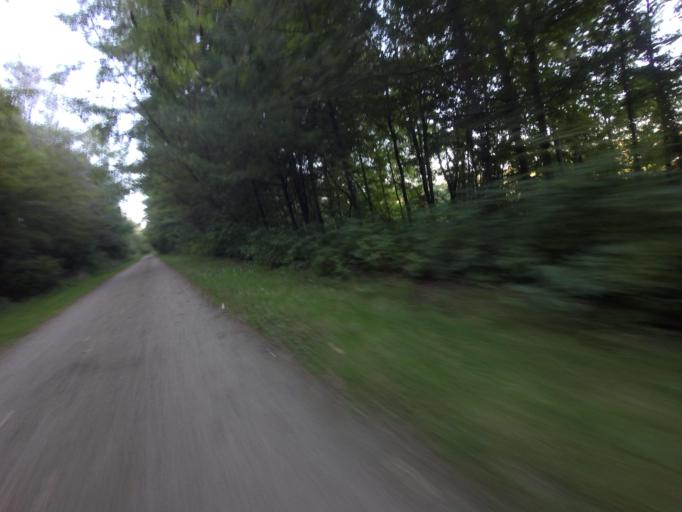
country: CA
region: Ontario
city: Goderich
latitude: 43.7562
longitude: -81.7129
